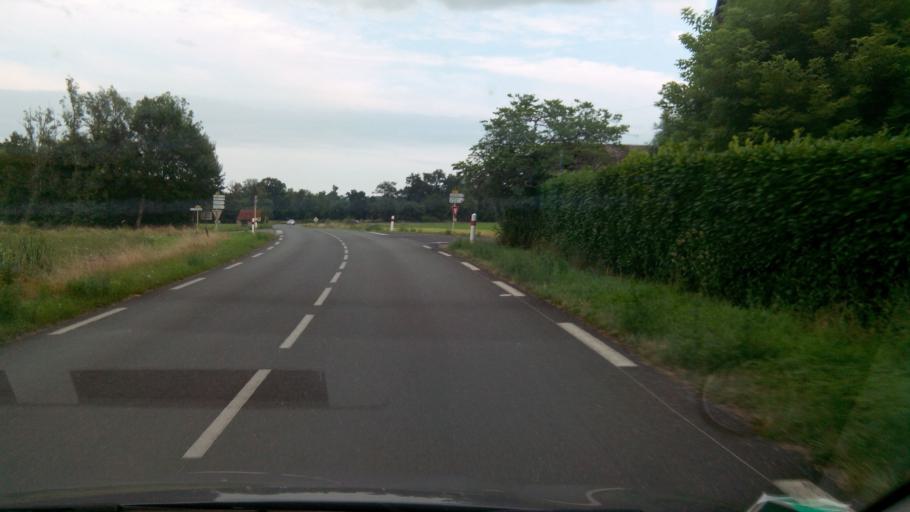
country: FR
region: Limousin
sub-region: Departement de la Correze
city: Meyssac
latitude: 45.0219
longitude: 1.6099
